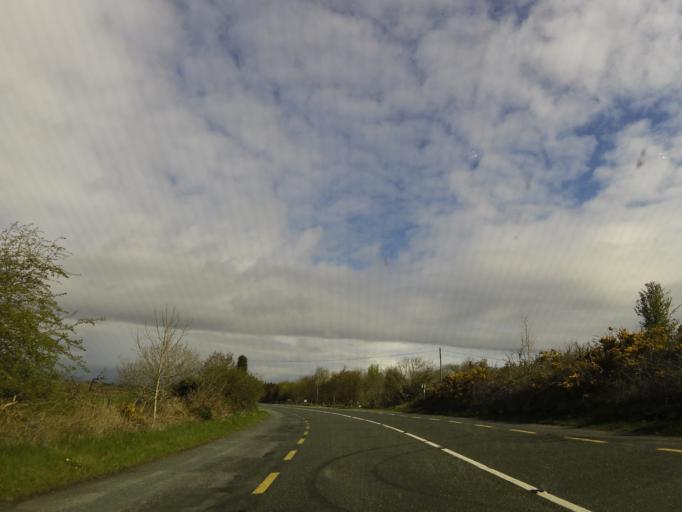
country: IE
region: Connaught
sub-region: Sligo
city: Tobercurry
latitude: 53.9417
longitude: -8.7904
